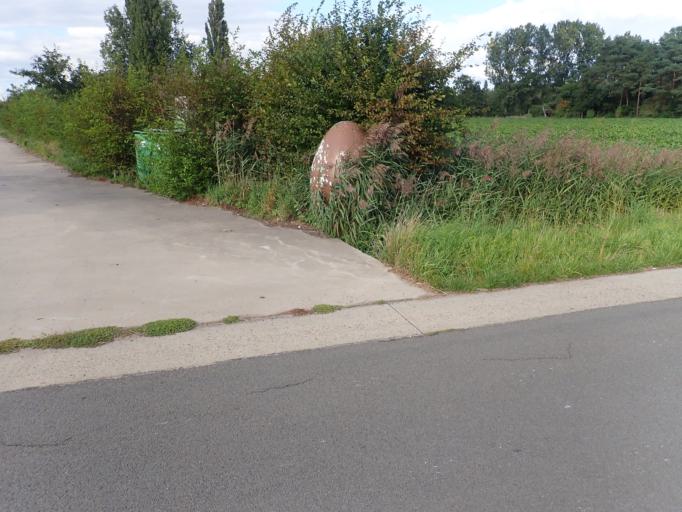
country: BE
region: Flanders
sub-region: Provincie Antwerpen
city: Lille
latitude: 51.2888
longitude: 4.7966
